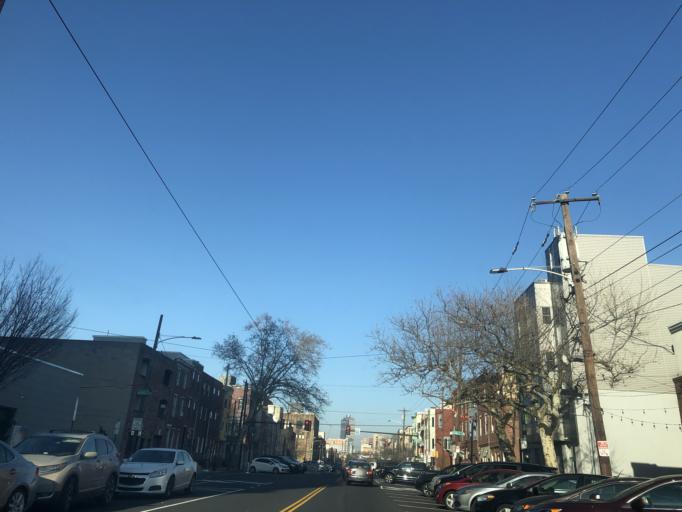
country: US
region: Pennsylvania
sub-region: Philadelphia County
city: Philadelphia
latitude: 39.9376
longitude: -75.1614
